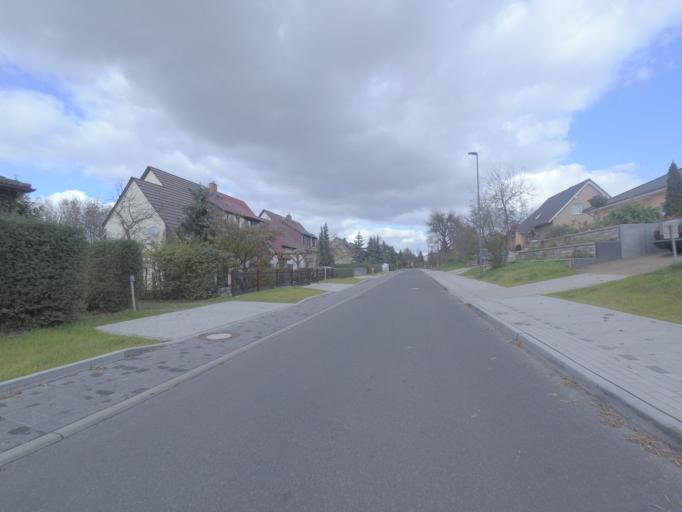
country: DE
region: Brandenburg
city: Ludwigsfelde
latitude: 52.2651
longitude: 13.3096
